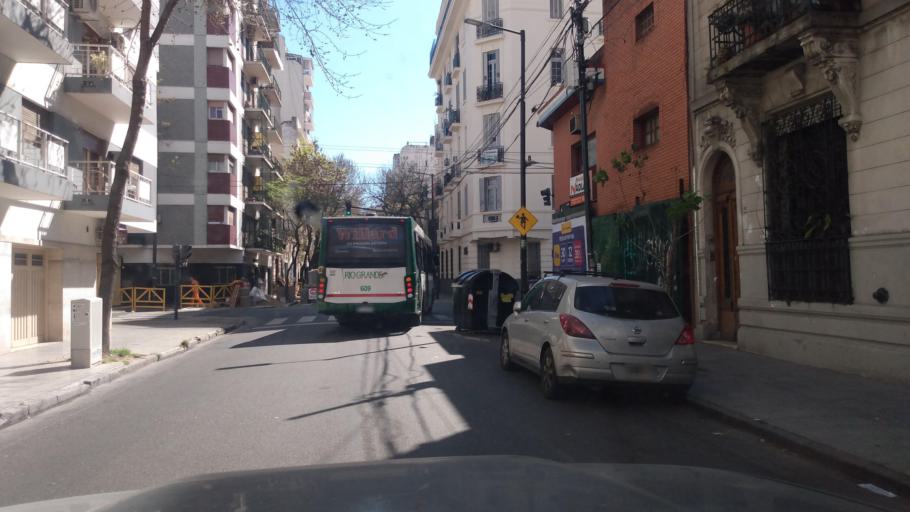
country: AR
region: Buenos Aires F.D.
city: Buenos Aires
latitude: -34.6174
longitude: -58.3945
